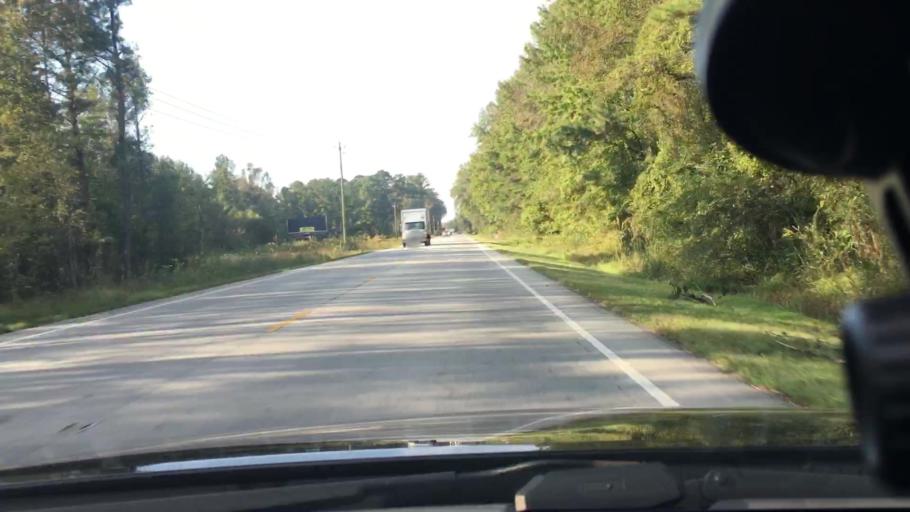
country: US
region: North Carolina
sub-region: Craven County
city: New Bern
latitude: 35.2098
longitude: -77.0610
